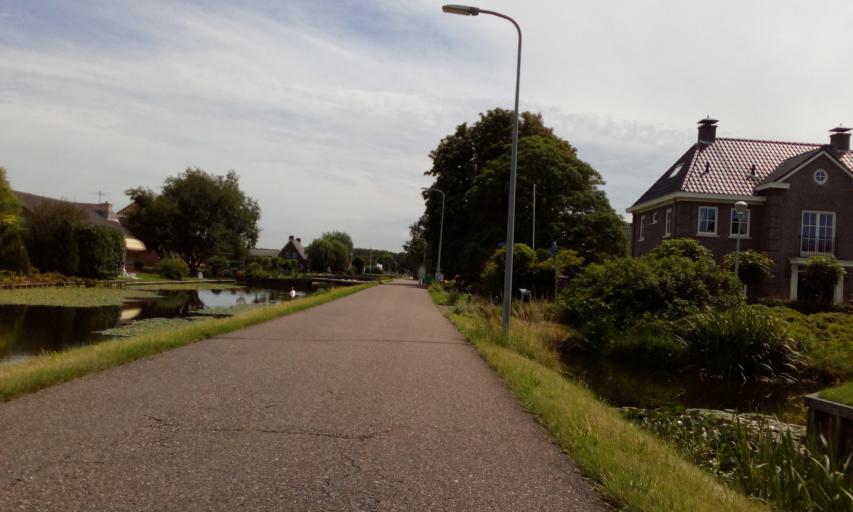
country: NL
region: South Holland
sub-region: Gemeente Den Haag
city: Ypenburg
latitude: 52.0376
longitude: 4.3887
